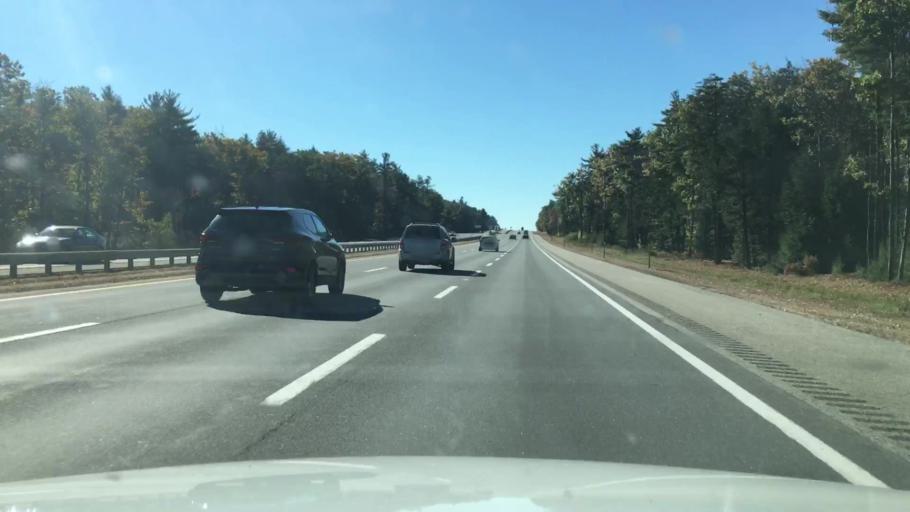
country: US
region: Maine
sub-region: York County
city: Ogunquit
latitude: 43.2885
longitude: -70.6170
